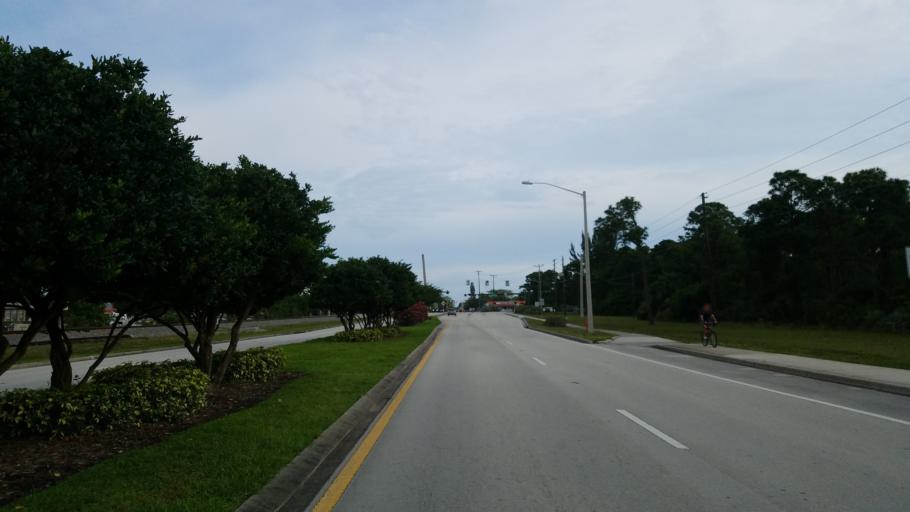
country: US
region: Florida
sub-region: Martin County
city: Stuart
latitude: 27.1798
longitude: -80.2347
